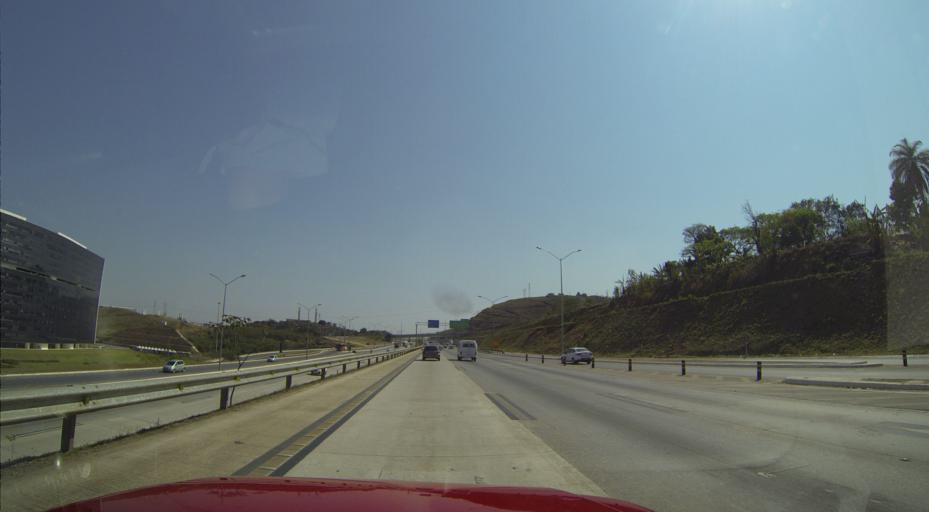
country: BR
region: Minas Gerais
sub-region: Vespasiano
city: Vespasiano
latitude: -19.7831
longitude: -43.9487
